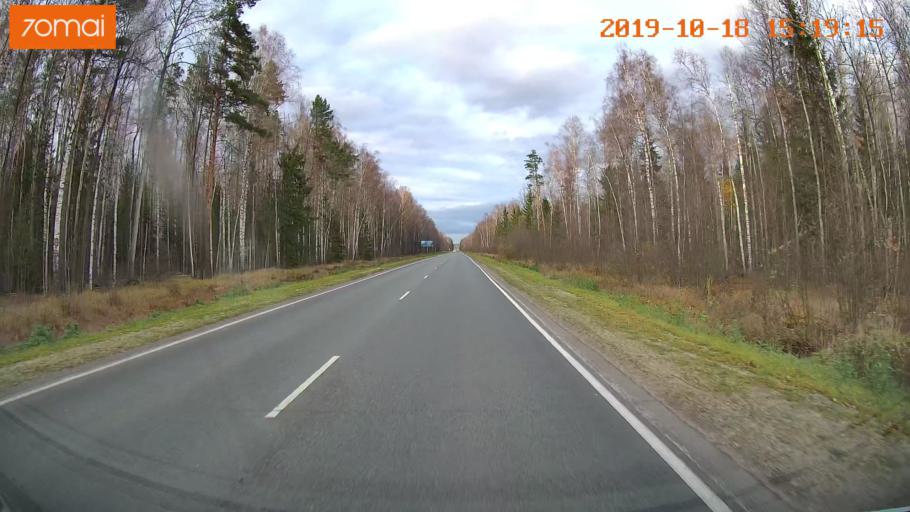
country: RU
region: Vladimir
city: Anopino
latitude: 55.6703
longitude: 40.7363
